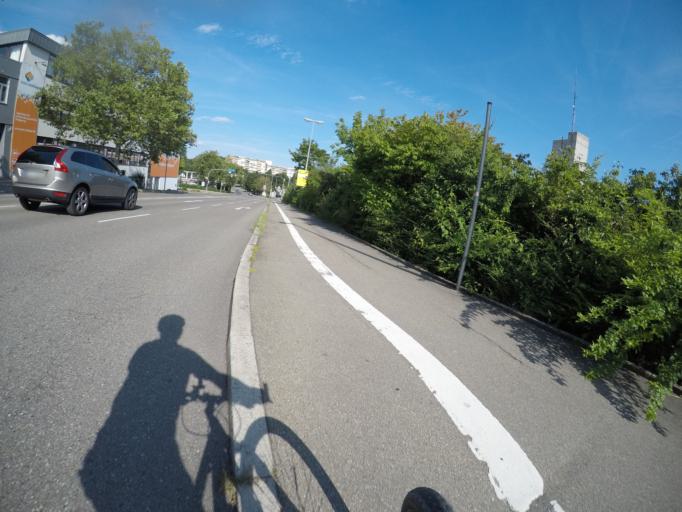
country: DE
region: Baden-Wuerttemberg
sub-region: Regierungsbezirk Stuttgart
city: Boeblingen
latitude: 48.6730
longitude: 9.0124
